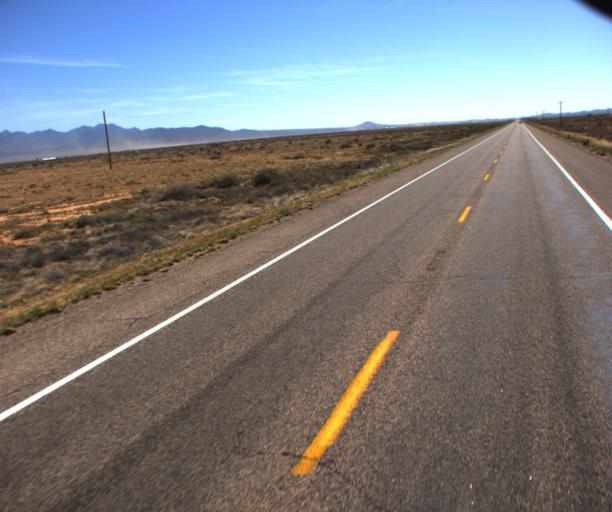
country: US
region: Arizona
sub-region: Mohave County
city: New Kingman-Butler
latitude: 35.3312
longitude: -113.9017
